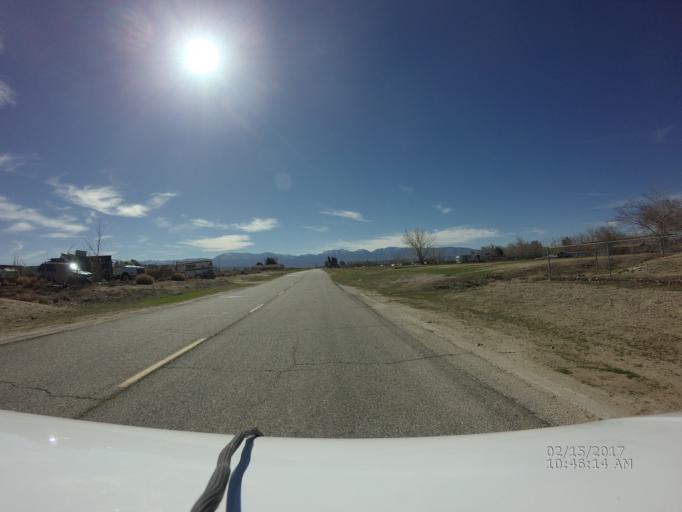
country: US
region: California
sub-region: Los Angeles County
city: Lake Los Angeles
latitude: 34.5828
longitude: -117.8534
